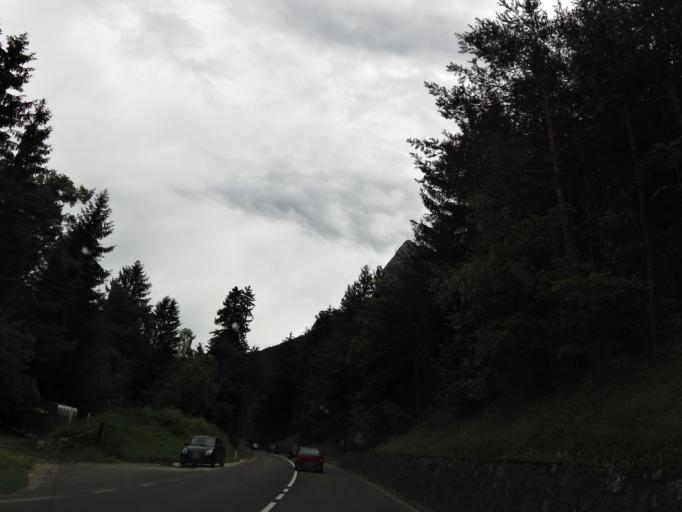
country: IT
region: Trentino-Alto Adige
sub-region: Bolzano
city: Siusi
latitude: 46.5311
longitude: 11.5338
